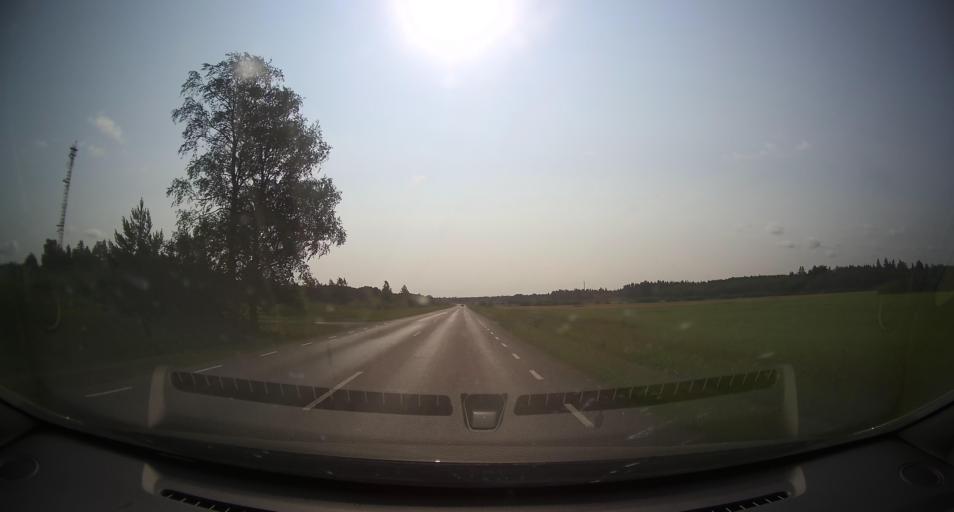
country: EE
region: Laeaene
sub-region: Lihula vald
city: Lihula
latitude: 58.5477
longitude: 23.8874
